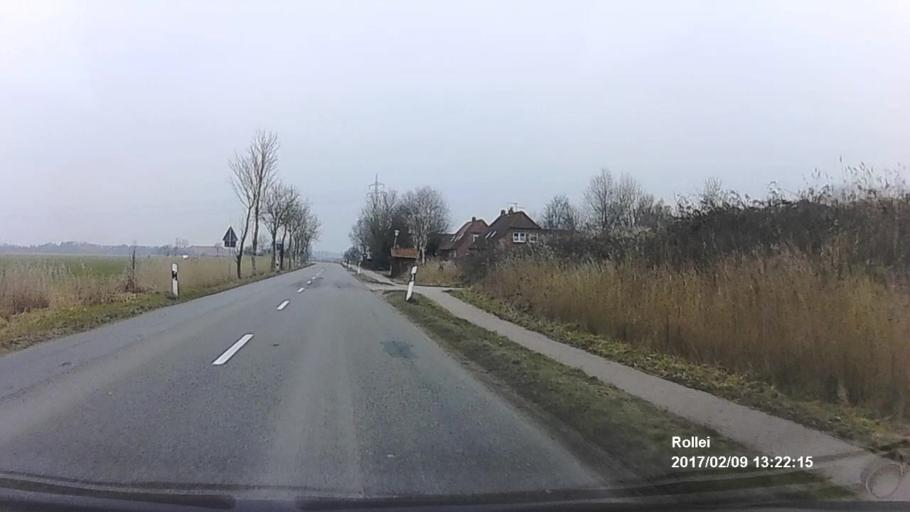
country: DE
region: Lower Saxony
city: Hinte
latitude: 53.4545
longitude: 7.1516
